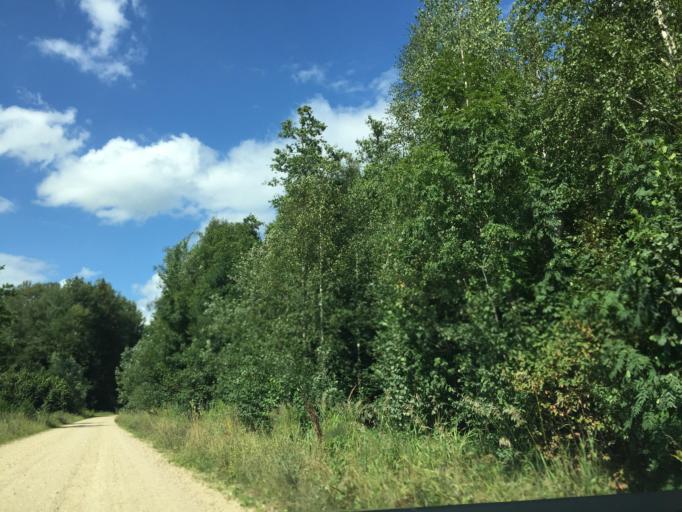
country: LV
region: Kegums
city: Kegums
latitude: 56.8223
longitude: 24.7466
